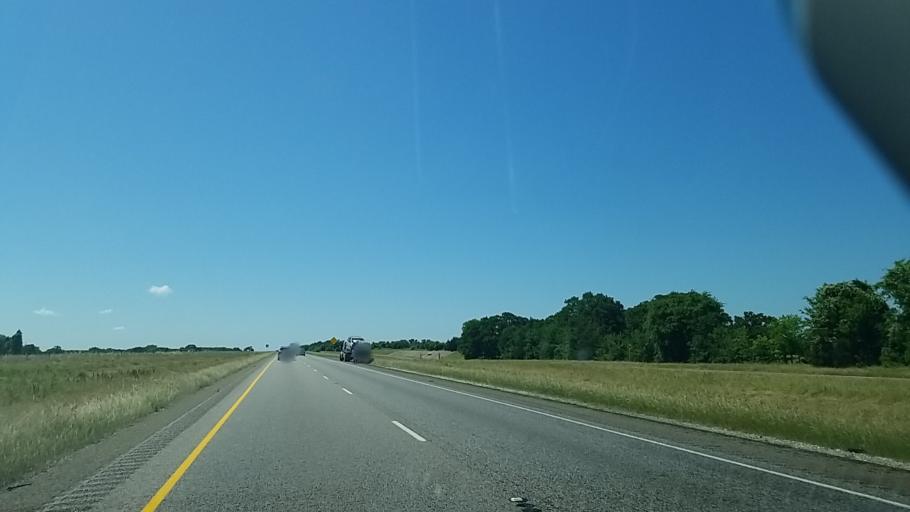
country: US
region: Texas
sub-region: Freestone County
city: Fairfield
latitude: 31.7689
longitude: -96.2186
